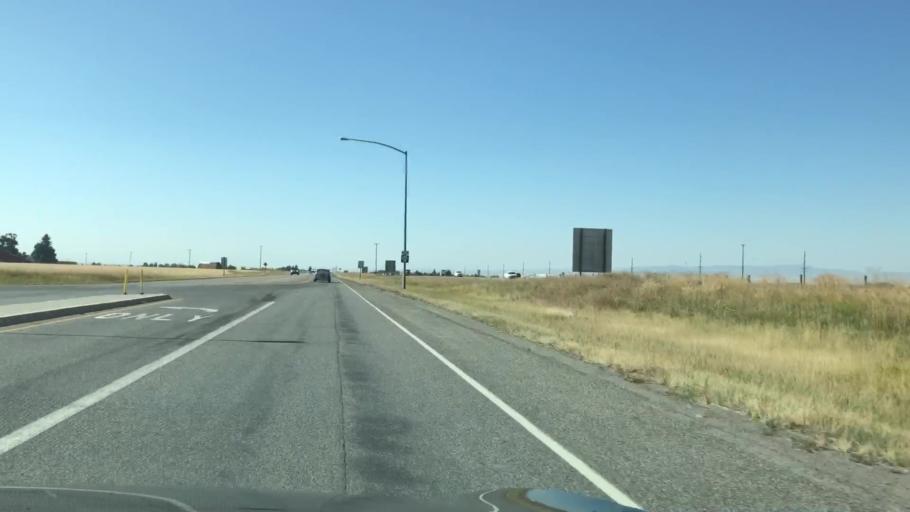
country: US
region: Montana
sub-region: Gallatin County
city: Bozeman
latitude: 45.7200
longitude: -111.0726
